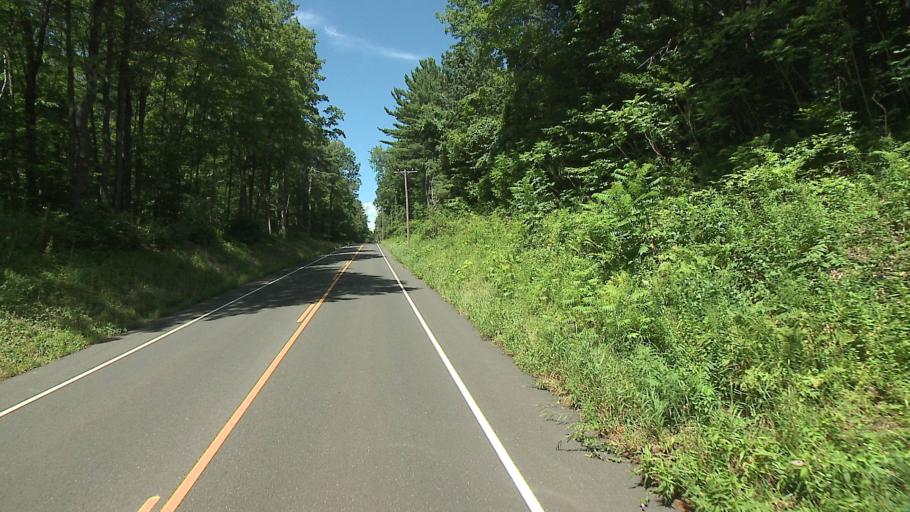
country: US
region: Connecticut
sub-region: Litchfield County
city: New Hartford Center
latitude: 41.9486
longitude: -72.9738
